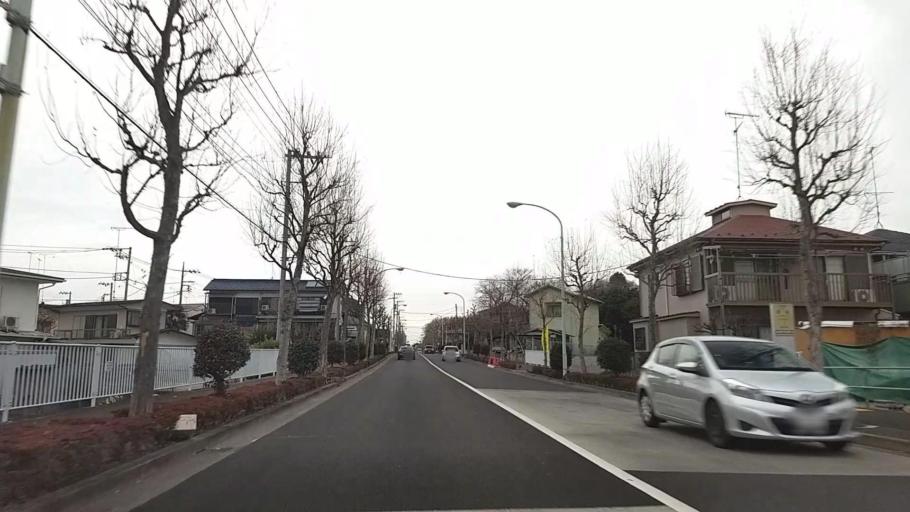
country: JP
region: Tokyo
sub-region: Machida-shi
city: Machida
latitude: 35.5193
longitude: 139.4639
